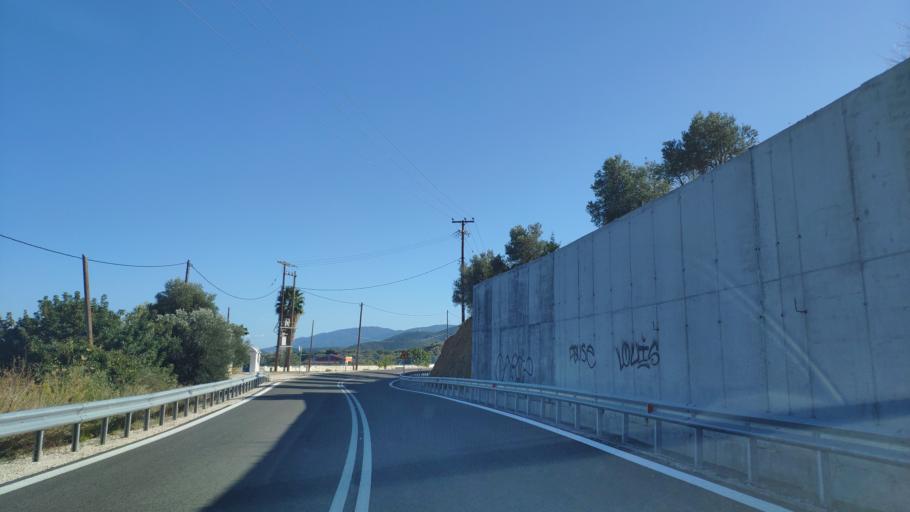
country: GR
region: Peloponnese
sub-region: Nomos Argolidos
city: Didyma
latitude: 37.5523
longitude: 23.2761
